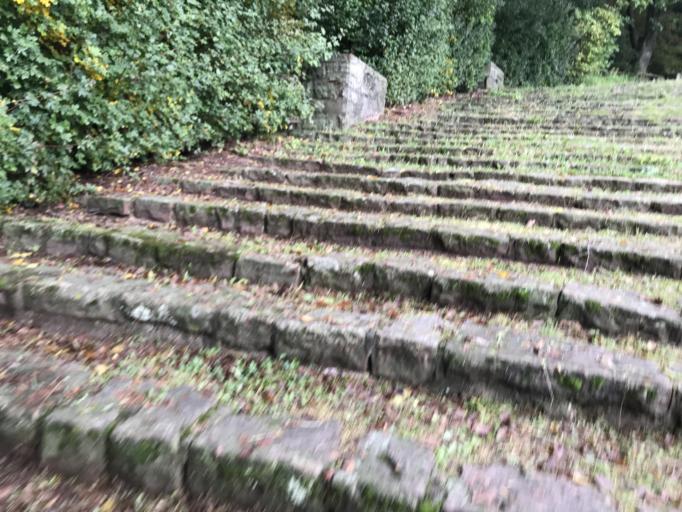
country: DE
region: Baden-Wuerttemberg
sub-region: Karlsruhe Region
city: Heidelberg
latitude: 49.4236
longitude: 8.7059
